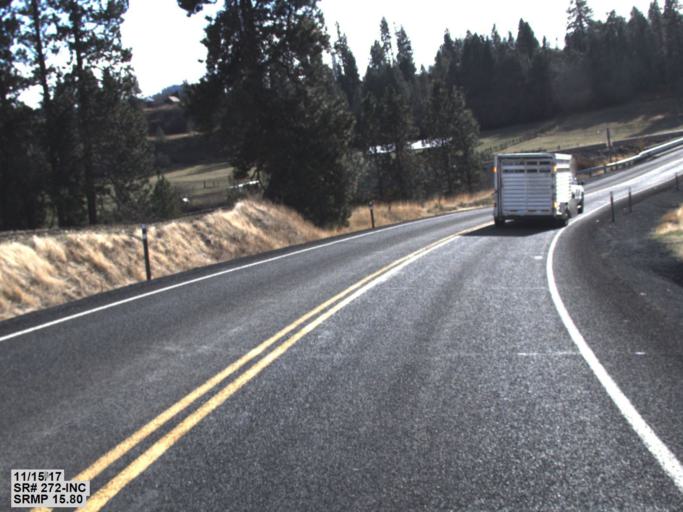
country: US
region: Idaho
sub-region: Latah County
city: Moscow
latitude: 46.9158
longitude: -117.0853
